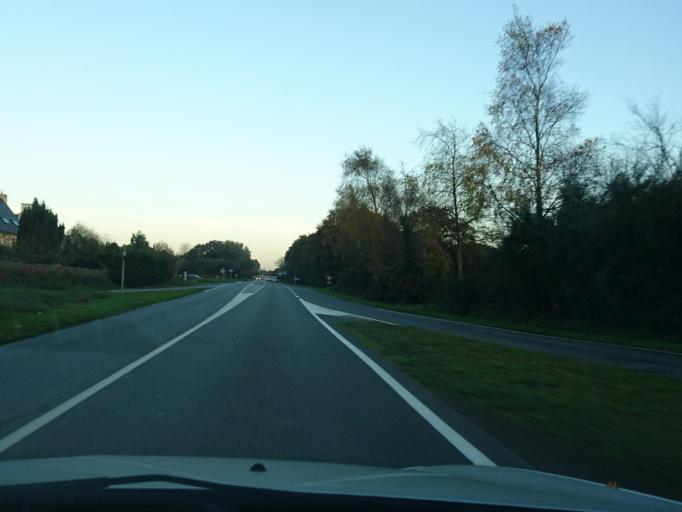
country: FR
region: Brittany
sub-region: Departement du Finistere
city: Saint-Renan
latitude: 48.4336
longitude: -4.6161
